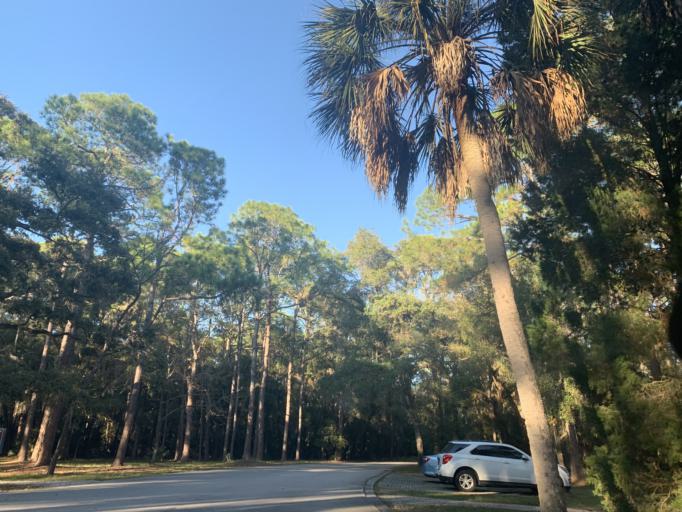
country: US
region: Florida
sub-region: Pinellas County
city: East Lake
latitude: 28.0962
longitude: -82.7092
